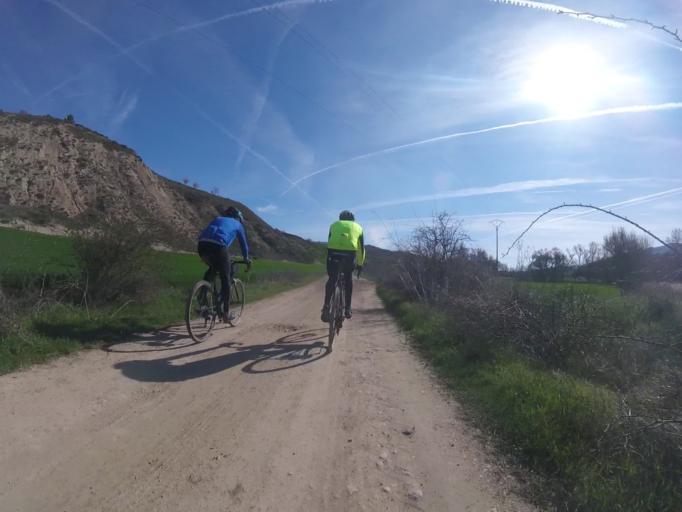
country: ES
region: Navarre
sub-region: Provincia de Navarra
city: Cirauqui
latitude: 42.6715
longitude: -1.9106
